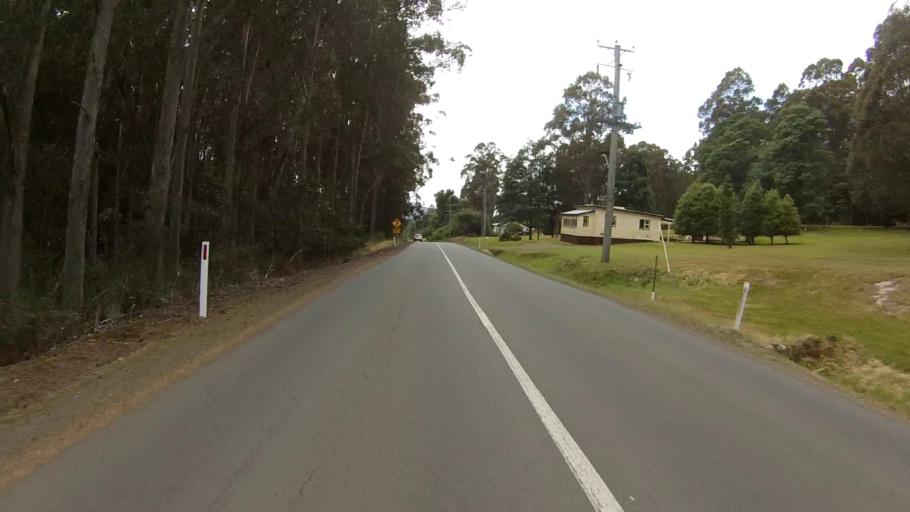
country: AU
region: Tasmania
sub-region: Kingborough
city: Kettering
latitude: -43.1168
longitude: 147.1889
